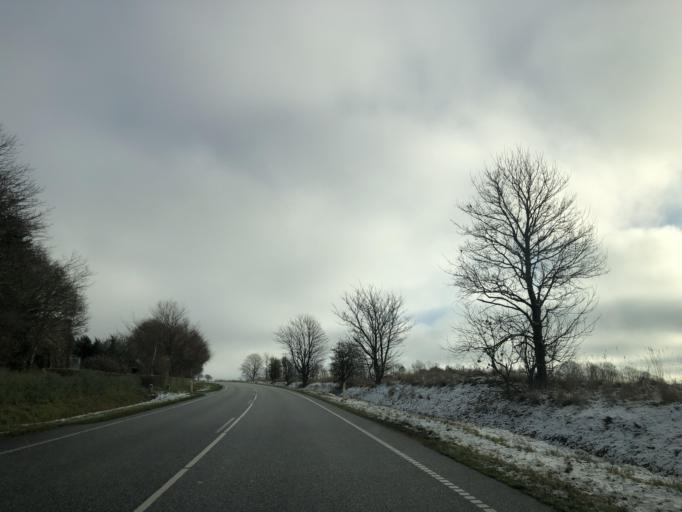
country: DK
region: Central Jutland
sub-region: Horsens Kommune
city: Braedstrup
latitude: 55.8979
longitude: 9.6202
